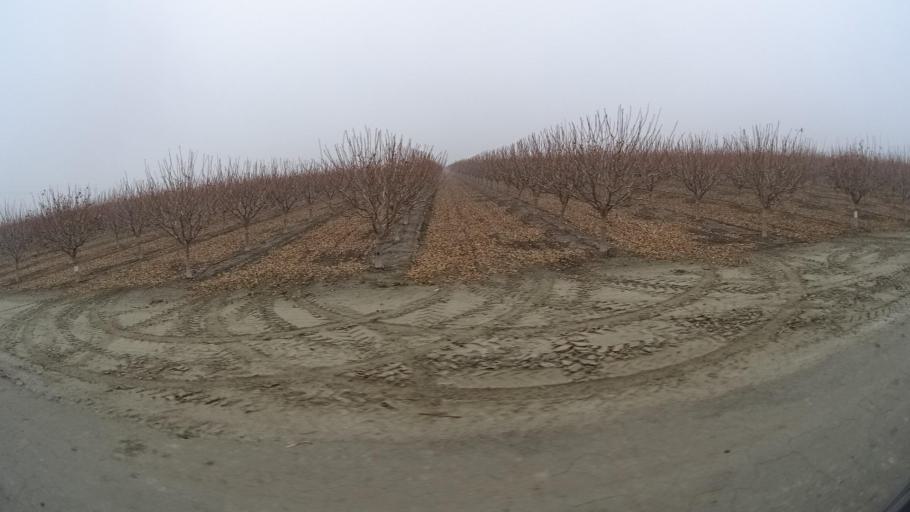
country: US
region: California
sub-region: Kern County
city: Buttonwillow
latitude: 35.4562
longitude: -119.5510
